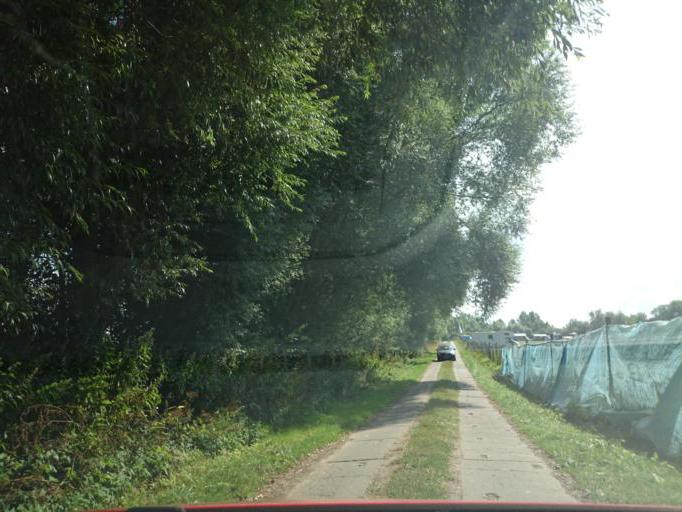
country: DE
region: Mecklenburg-Vorpommern
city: Barth
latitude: 54.3670
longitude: 12.7552
